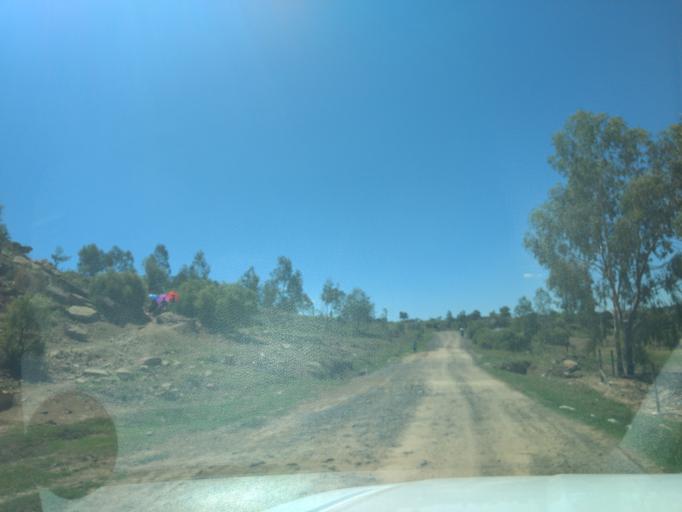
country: LS
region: Maseru
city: Maseru
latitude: -29.4921
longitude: 27.3710
